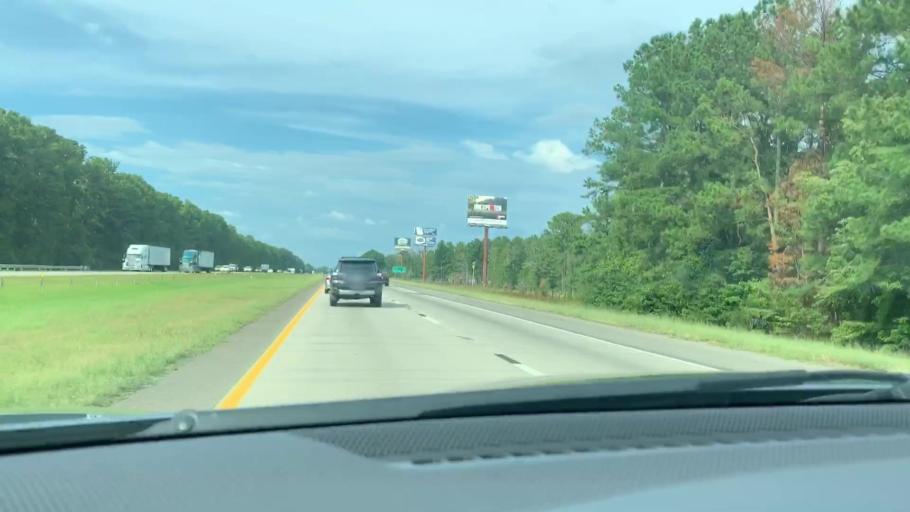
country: US
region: South Carolina
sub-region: Colleton County
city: Walterboro
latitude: 32.9419
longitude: -80.6848
